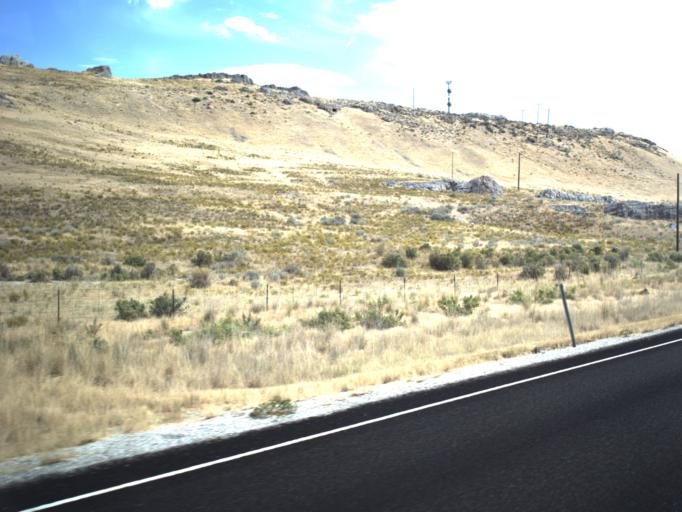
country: US
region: Utah
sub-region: Box Elder County
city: Tremonton
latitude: 41.6178
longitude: -112.3824
